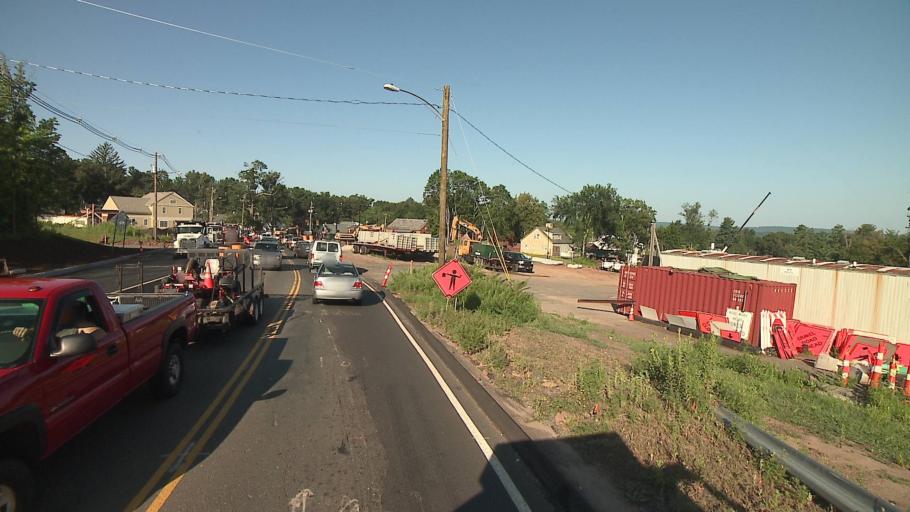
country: US
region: Connecticut
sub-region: Hartford County
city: Farmington
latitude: 41.7261
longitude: -72.8209
